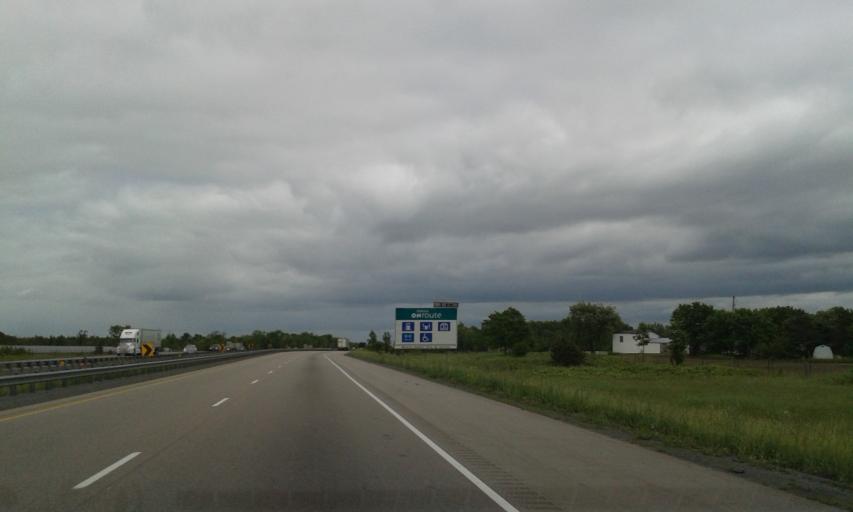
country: CA
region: Ontario
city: Kingston
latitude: 44.2842
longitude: -76.6917
